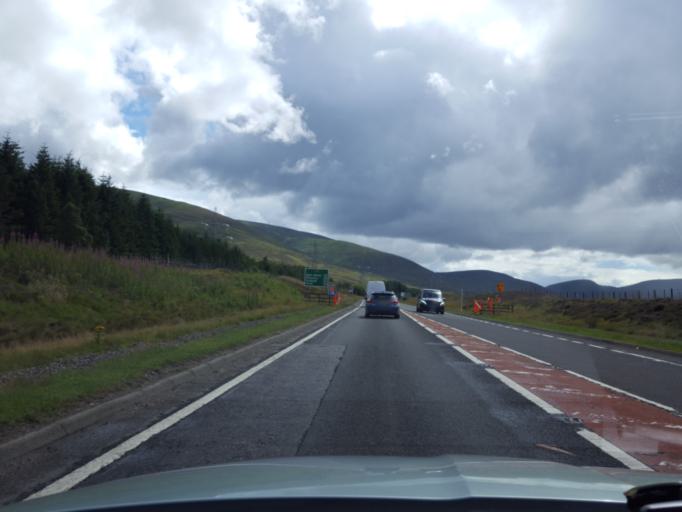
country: GB
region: Scotland
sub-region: Highland
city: Kingussie
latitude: 56.9161
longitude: -4.2357
